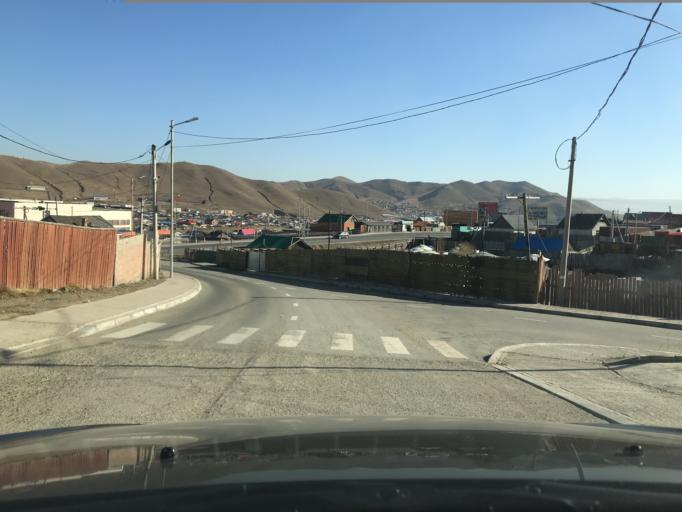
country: MN
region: Ulaanbaatar
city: Ulaanbaatar
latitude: 47.9955
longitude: 106.9244
